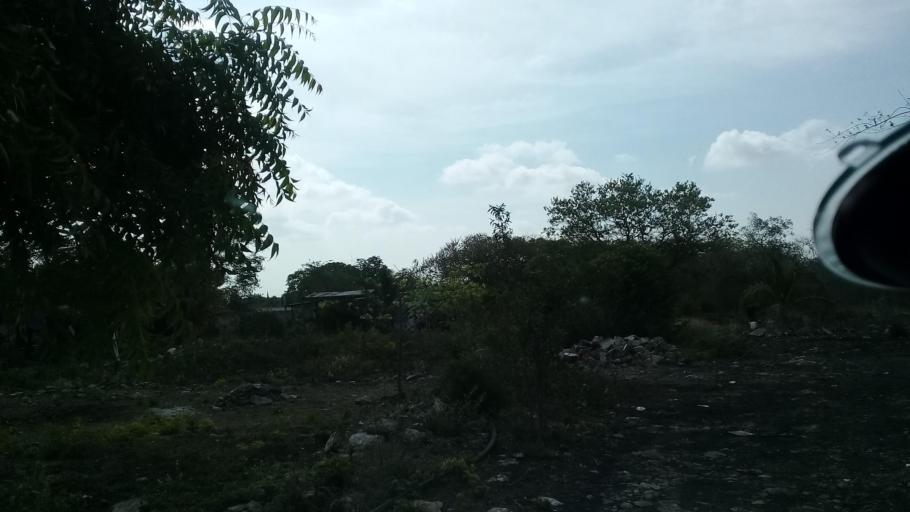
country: MX
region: Veracruz
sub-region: Emiliano Zapata
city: Plan del Rio
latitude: 19.3881
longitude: -96.6378
